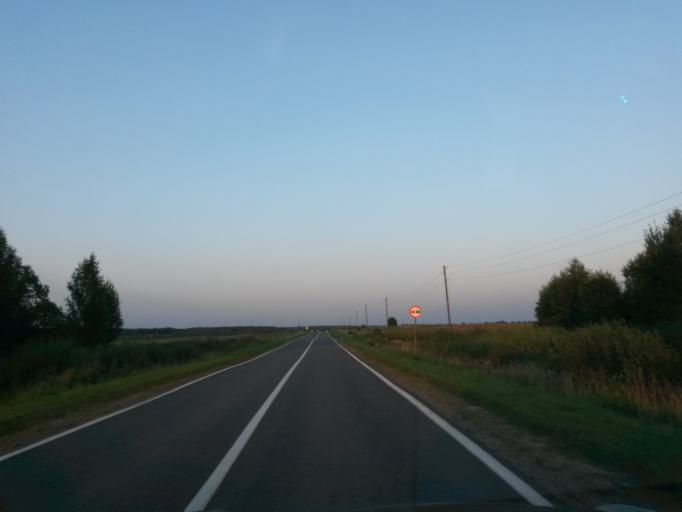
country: RU
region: Jaroslavl
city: Tutayev
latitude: 57.9490
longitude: 39.4596
